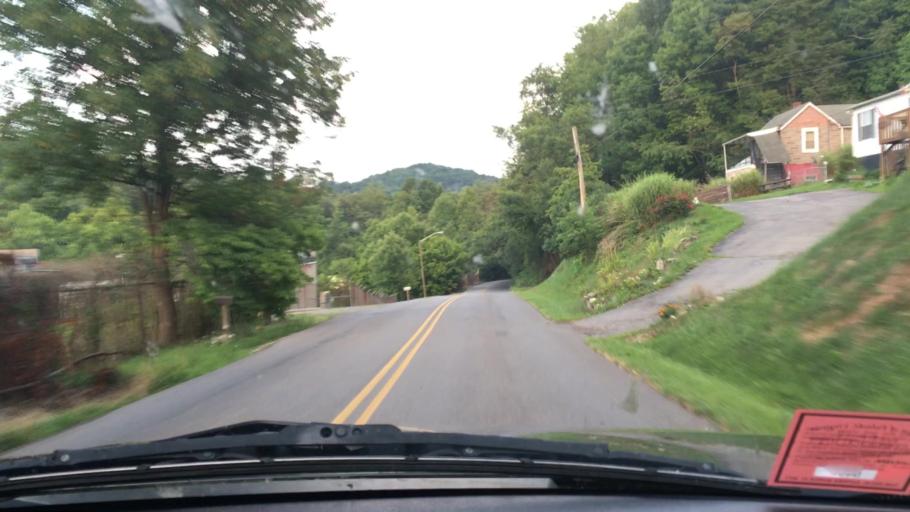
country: US
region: Virginia
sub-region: Pulaski County
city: Pulaski
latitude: 37.0428
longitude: -80.7493
